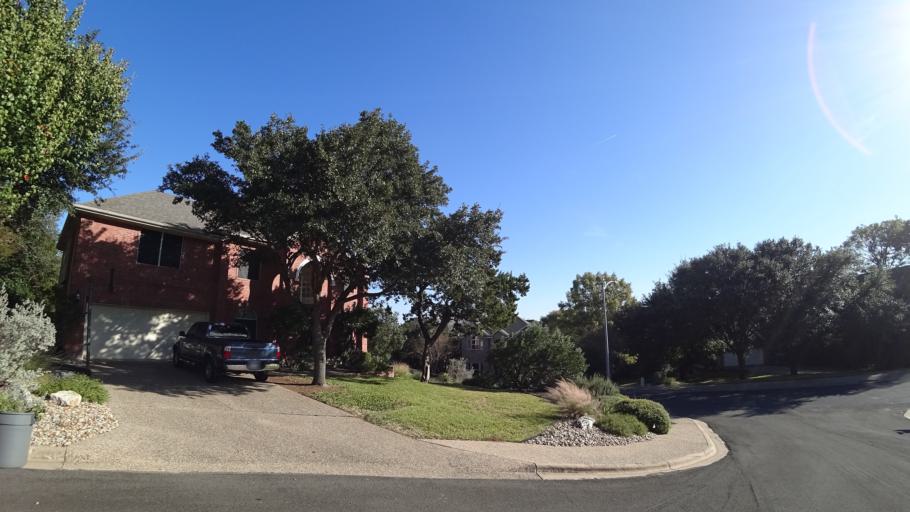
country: US
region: Texas
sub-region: Williamson County
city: Jollyville
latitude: 30.4137
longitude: -97.7763
